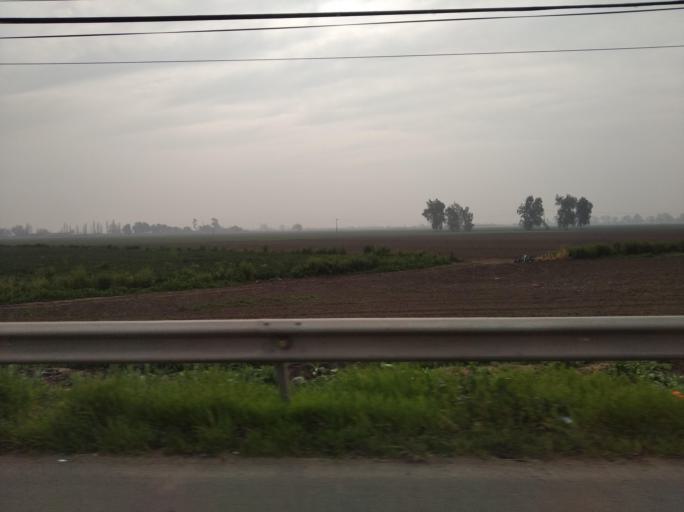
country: CL
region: Santiago Metropolitan
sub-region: Provincia de Chacabuco
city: Lampa
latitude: -33.3407
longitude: -70.8130
